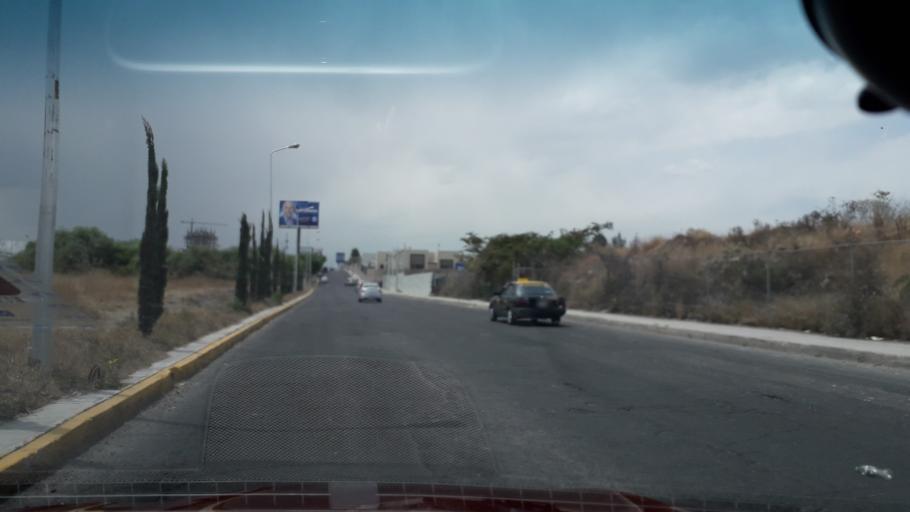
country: MX
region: Puebla
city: Puebla
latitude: 19.0198
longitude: -98.2360
